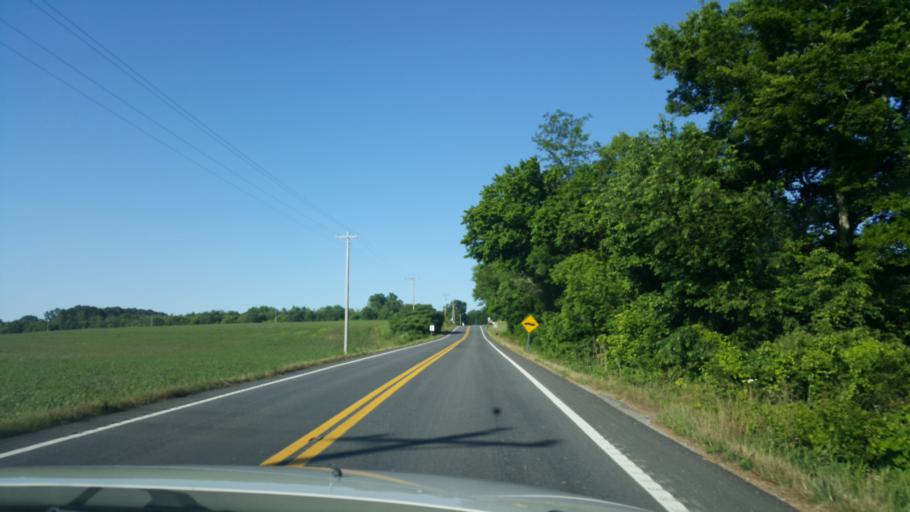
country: US
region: Tennessee
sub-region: Lawrence County
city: Lawrenceburg
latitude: 35.3965
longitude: -87.3885
